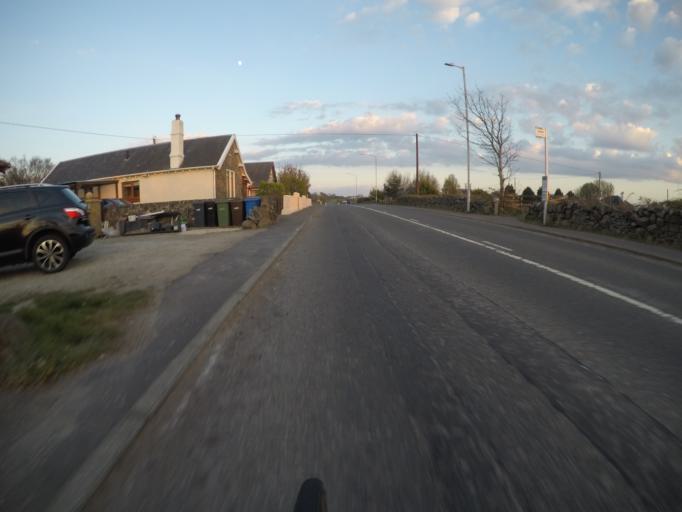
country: GB
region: Scotland
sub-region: South Ayrshire
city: Troon
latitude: 55.5596
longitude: -4.6303
